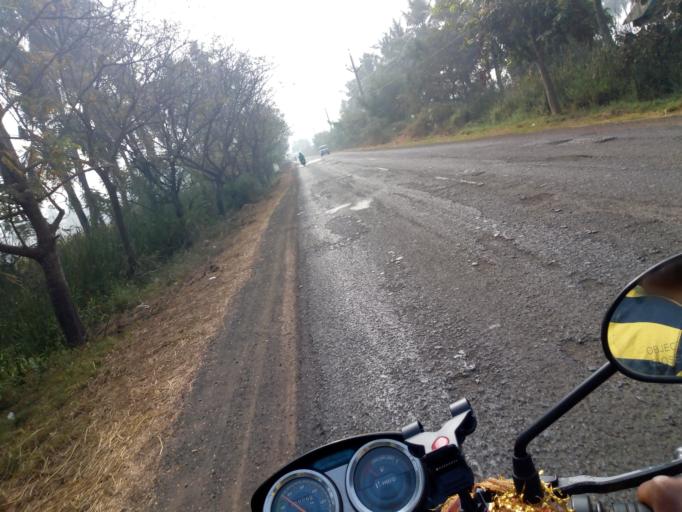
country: IN
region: Andhra Pradesh
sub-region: West Godavari
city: Tadepallegudem
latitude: 16.7936
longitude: 81.4170
